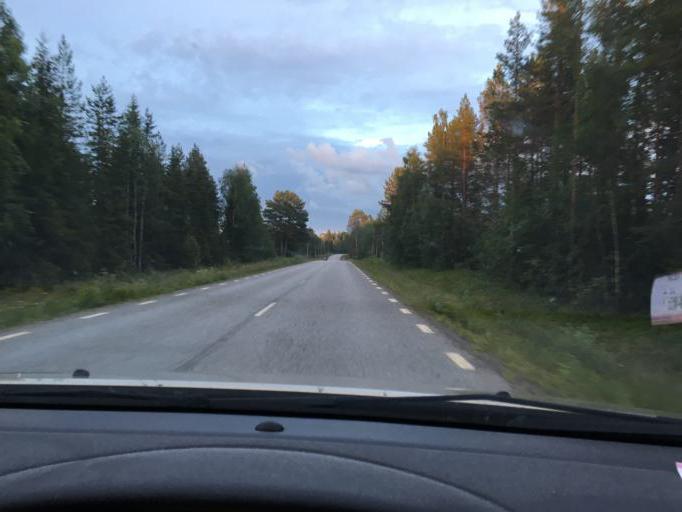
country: SE
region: Norrbotten
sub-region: Lulea Kommun
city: Ranea
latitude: 66.0472
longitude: 22.2786
